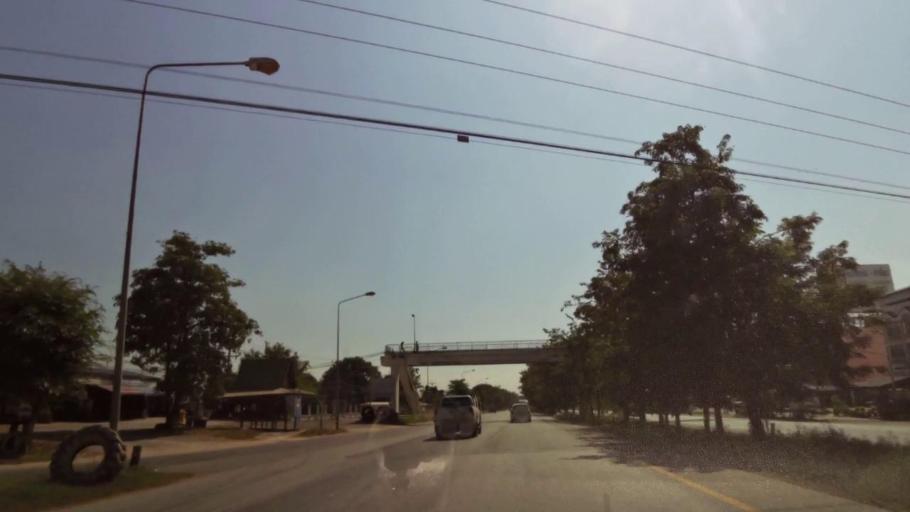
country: TH
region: Nakhon Sawan
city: Kao Liao
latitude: 15.8698
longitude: 100.1166
